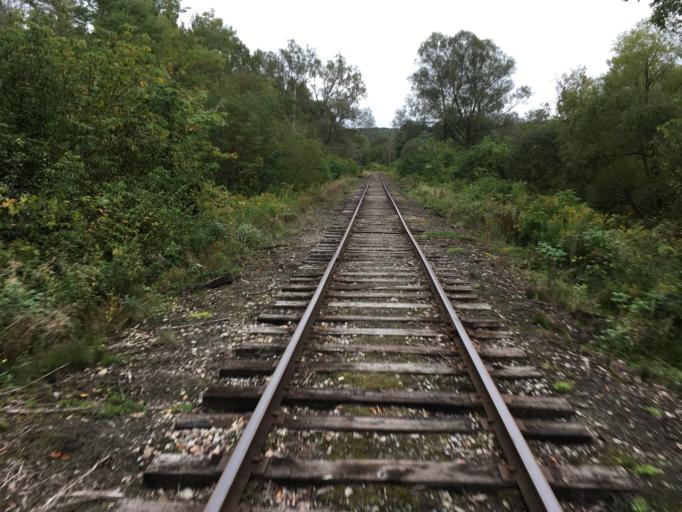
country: US
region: Vermont
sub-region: Washington County
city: Montpelier
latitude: 44.2377
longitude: -72.5497
